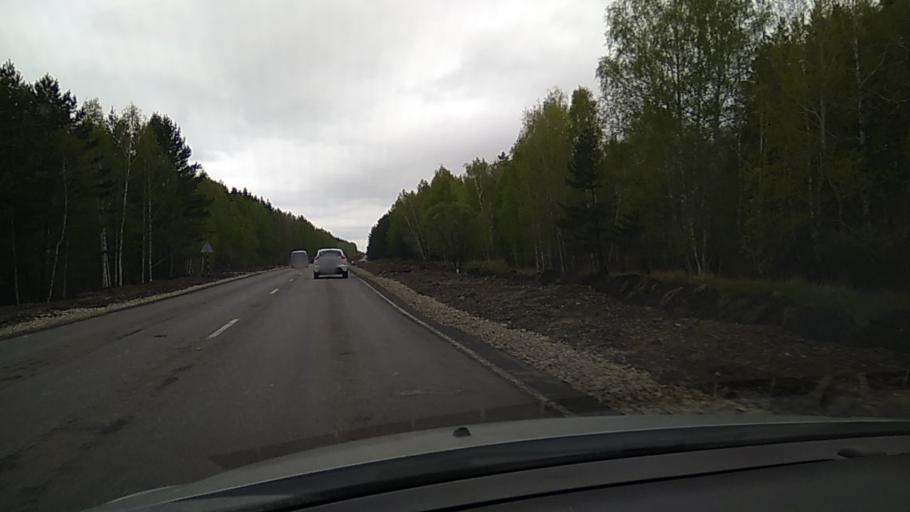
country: RU
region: Kurgan
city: Shadrinsk
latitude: 56.1422
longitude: 63.5138
